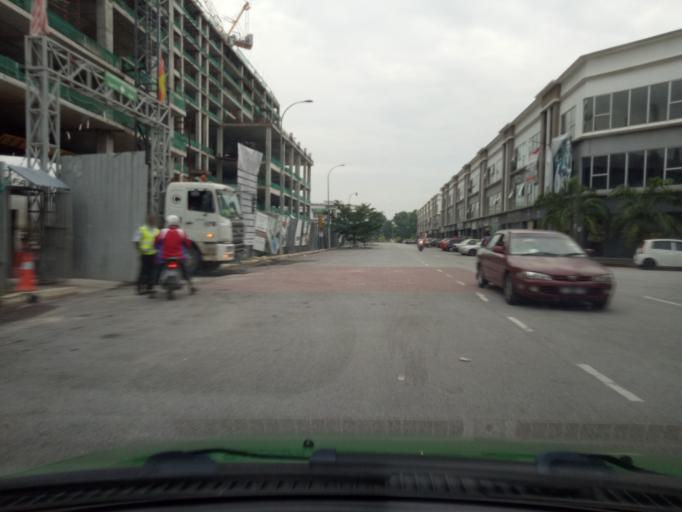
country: MY
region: Selangor
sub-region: Hulu Langat
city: Semenyih
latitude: 2.9269
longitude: 101.8595
